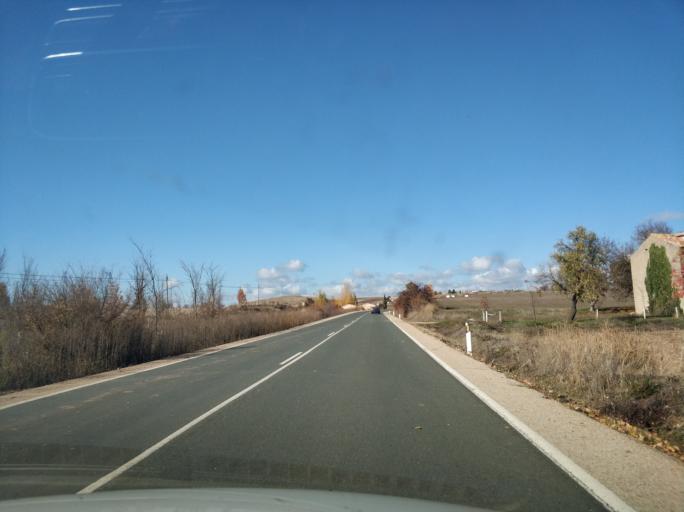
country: ES
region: Castille and Leon
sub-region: Provincia de Soria
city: Almazan
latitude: 41.4735
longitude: -2.5288
